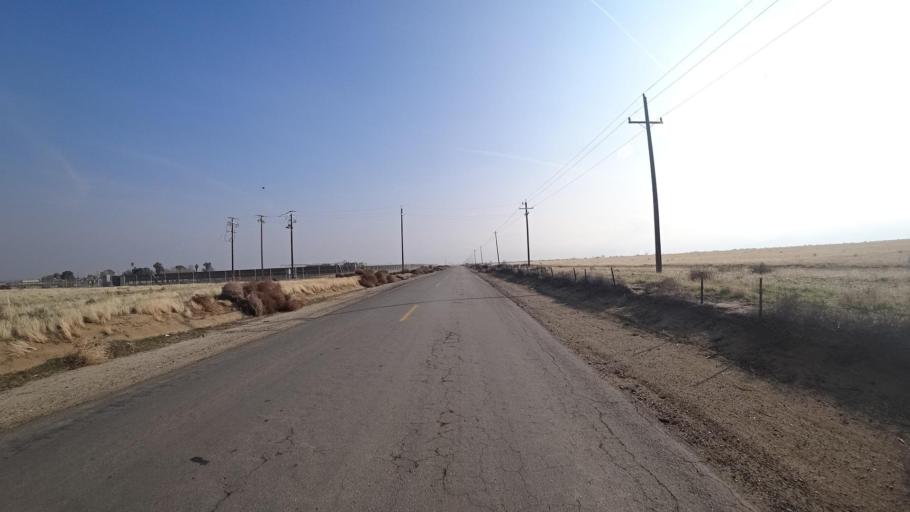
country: US
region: California
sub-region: Kern County
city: Lebec
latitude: 34.9844
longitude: -118.9144
